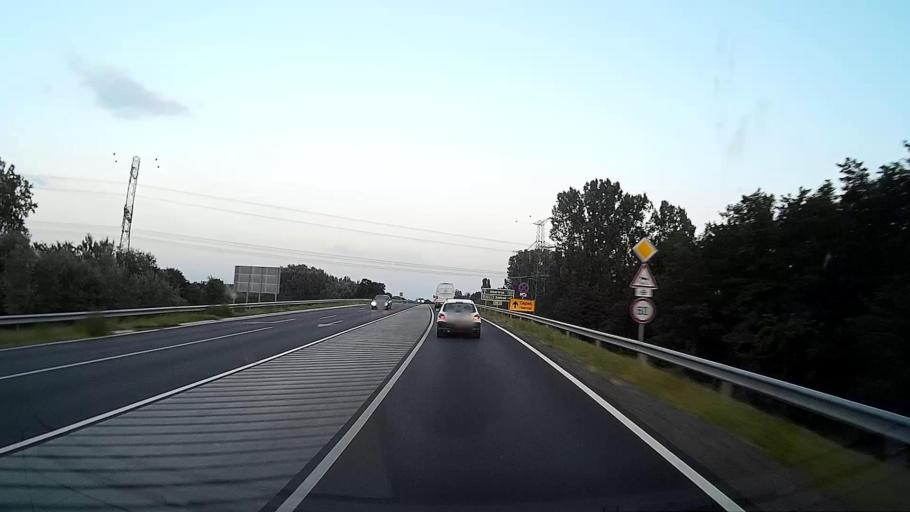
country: HU
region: Pest
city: Albertirsa
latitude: 47.2615
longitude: 19.5839
